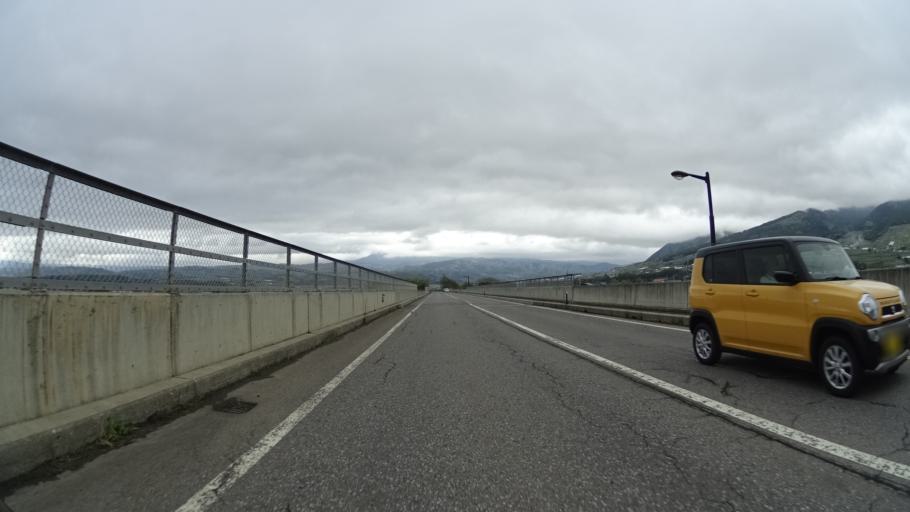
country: JP
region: Nagano
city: Nakano
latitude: 36.7578
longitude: 138.3915
